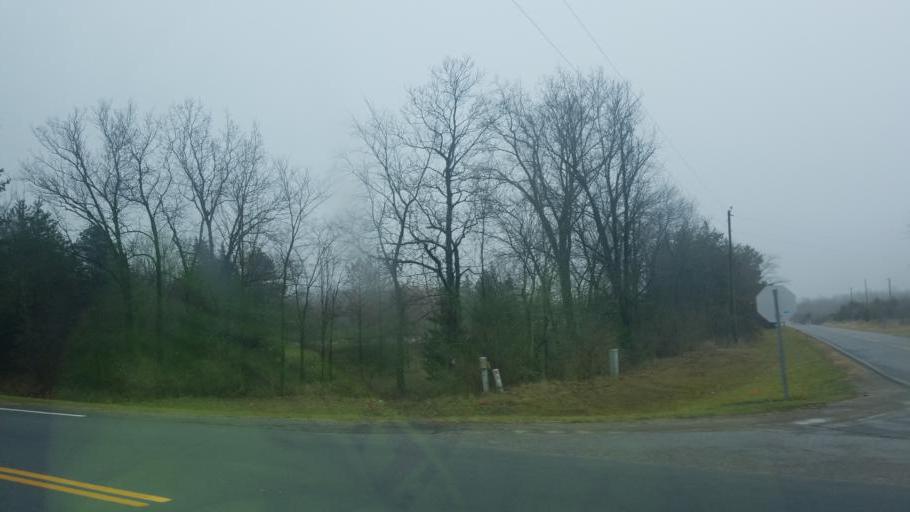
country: US
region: Ohio
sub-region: Champaign County
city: North Lewisburg
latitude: 40.2635
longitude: -83.4693
